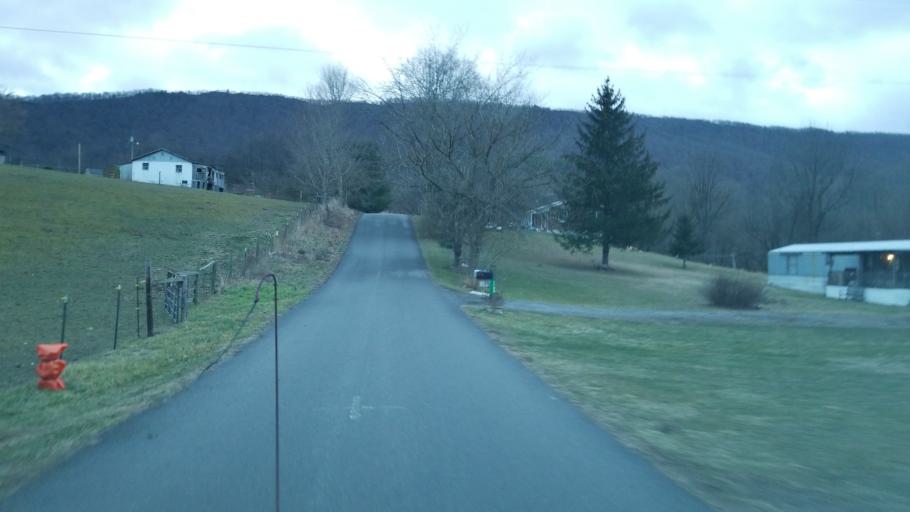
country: US
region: Virginia
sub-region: Pulaski County
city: Pulaski
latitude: 37.1598
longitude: -80.8672
